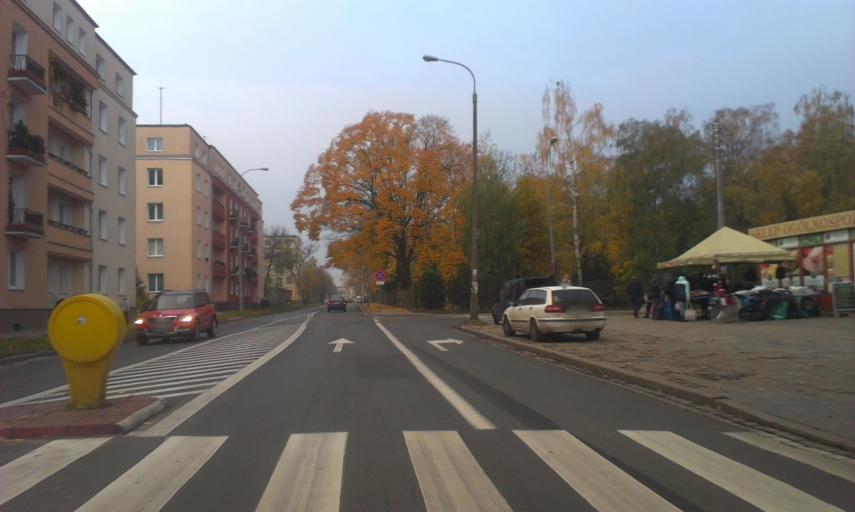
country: PL
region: Greater Poland Voivodeship
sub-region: Poznan
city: Poznan
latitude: 52.4162
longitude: 16.8813
